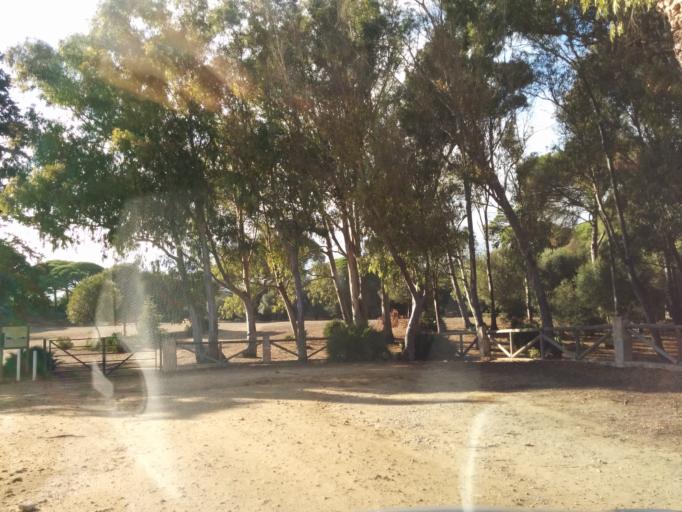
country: ES
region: Andalusia
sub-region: Provincia de Cadiz
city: Vejer de la Frontera
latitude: 36.1971
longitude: -5.9820
